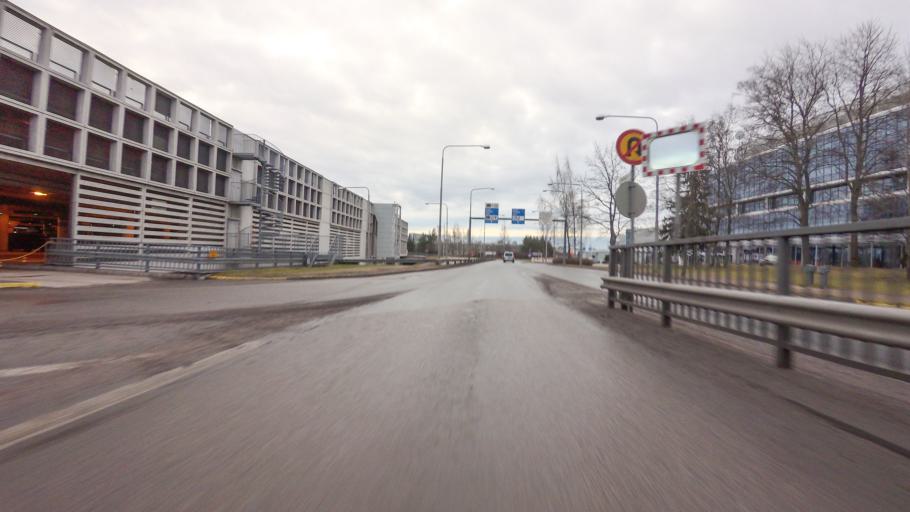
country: FI
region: Uusimaa
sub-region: Helsinki
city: Vantaa
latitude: 60.3170
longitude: 24.9665
